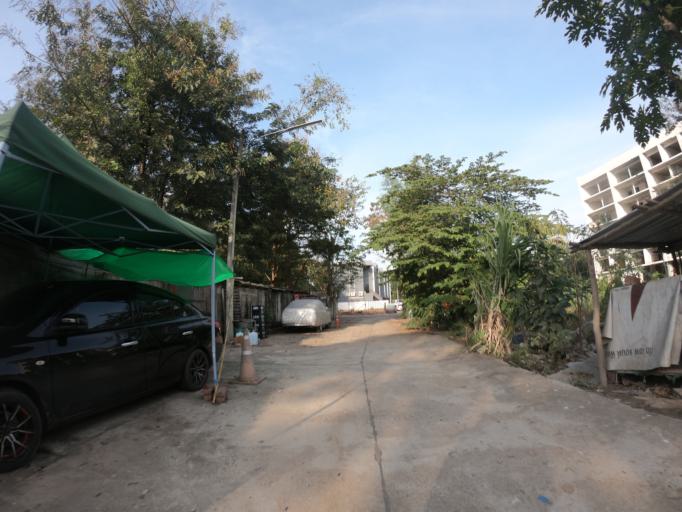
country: TH
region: Chiang Mai
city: Chiang Mai
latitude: 18.8216
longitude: 98.9635
